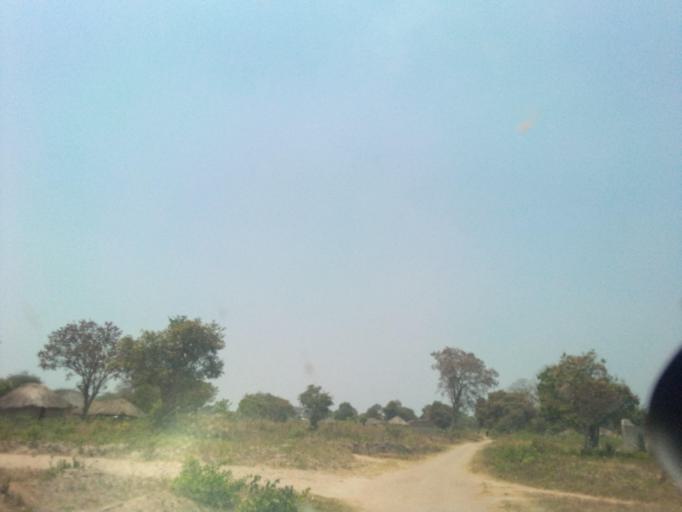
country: ZM
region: Copperbelt
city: Kataba
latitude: -12.2422
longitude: 30.3200
